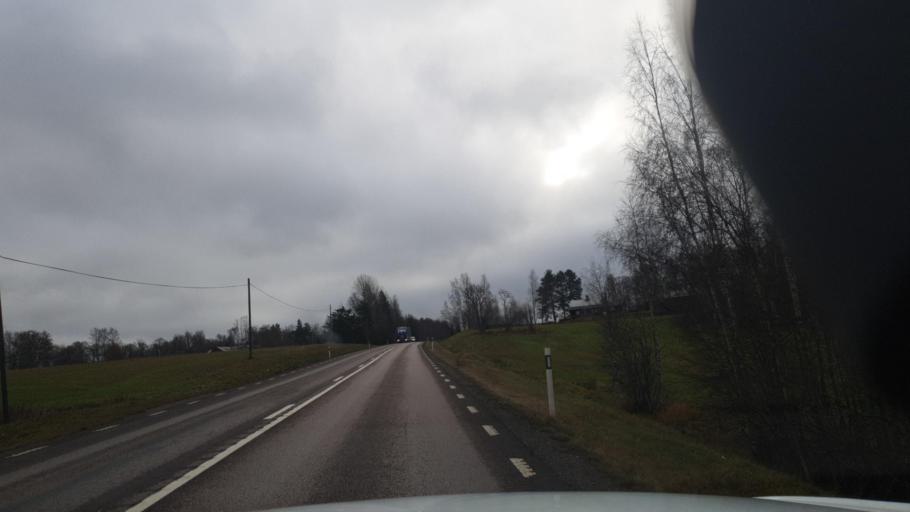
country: SE
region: Vaermland
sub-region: Karlstads Kommun
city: Edsvalla
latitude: 59.5773
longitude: 13.0189
